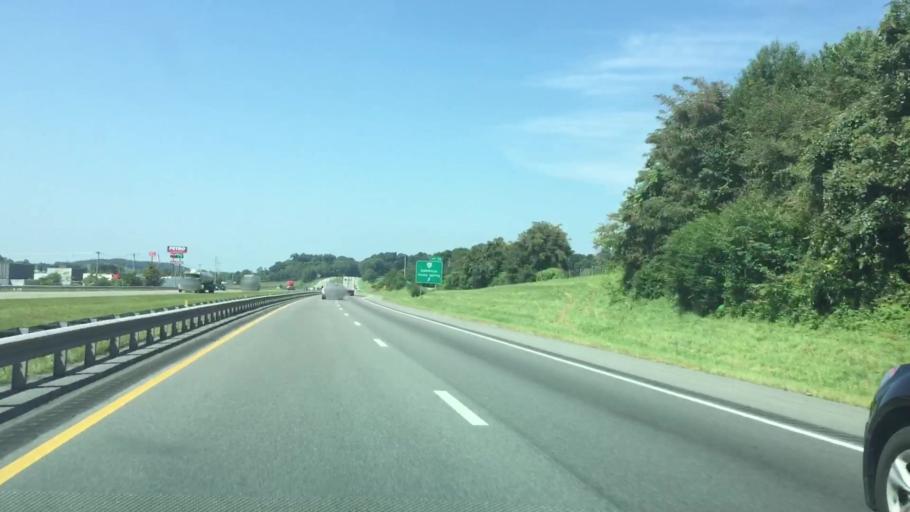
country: US
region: Virginia
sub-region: Washington County
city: Glade Spring
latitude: 36.7741
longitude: -81.7746
